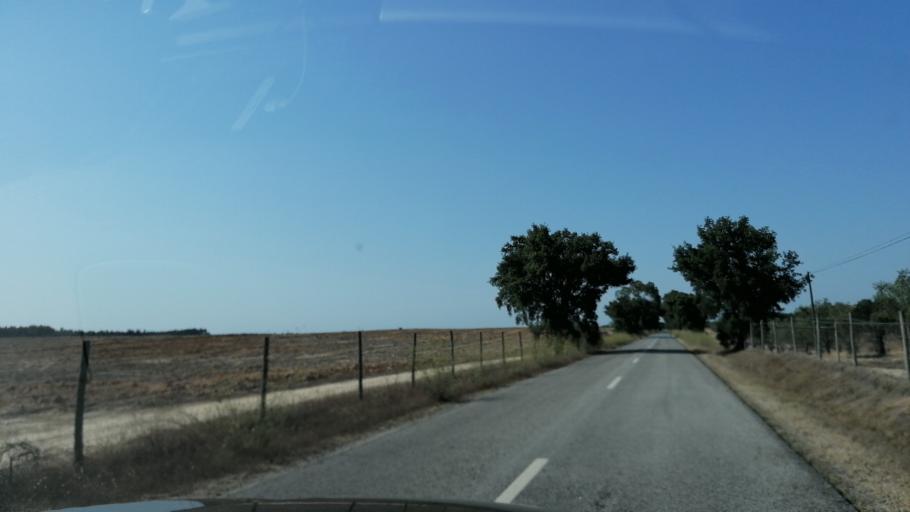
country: PT
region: Evora
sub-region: Vendas Novas
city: Vendas Novas
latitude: 38.7284
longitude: -8.6224
